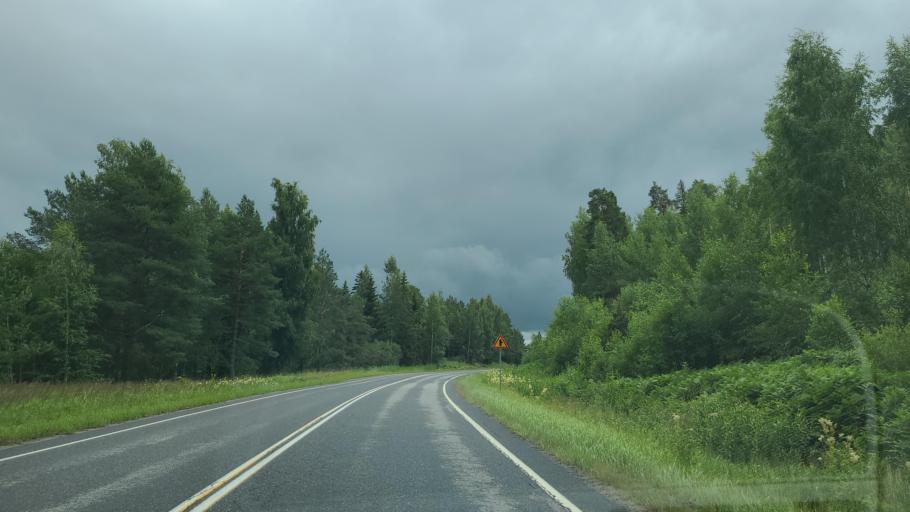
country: FI
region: Varsinais-Suomi
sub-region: Turku
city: Sauvo
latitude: 60.3388
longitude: 22.7007
